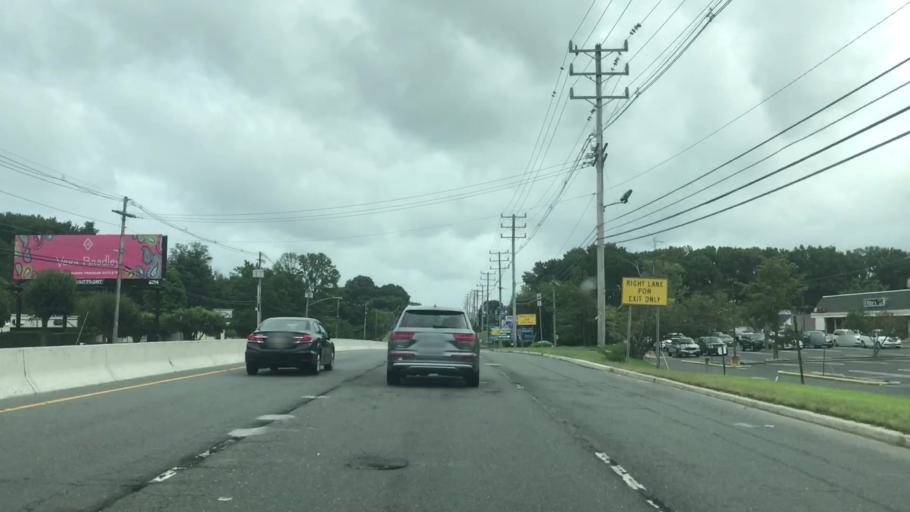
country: US
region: New Jersey
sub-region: Monmouth County
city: Oakhurst
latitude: 40.2569
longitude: -74.0405
